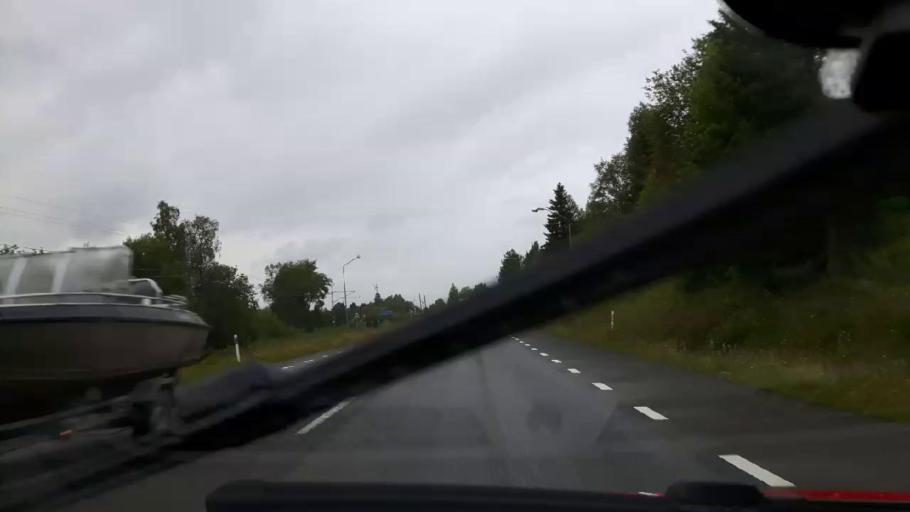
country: SE
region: Jaemtland
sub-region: Are Kommun
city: Jarpen
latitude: 63.3100
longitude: 13.6122
